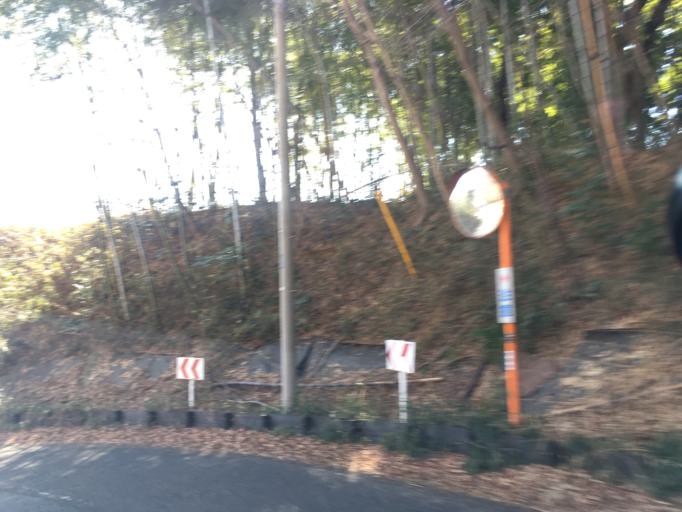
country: JP
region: Tokyo
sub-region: Machida-shi
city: Machida
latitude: 35.5835
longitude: 139.4160
